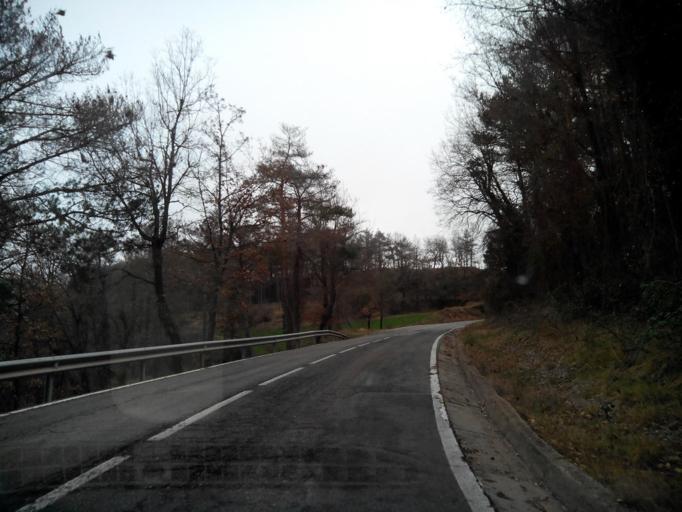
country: ES
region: Catalonia
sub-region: Provincia de Barcelona
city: Olost
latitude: 41.9692
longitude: 2.1383
